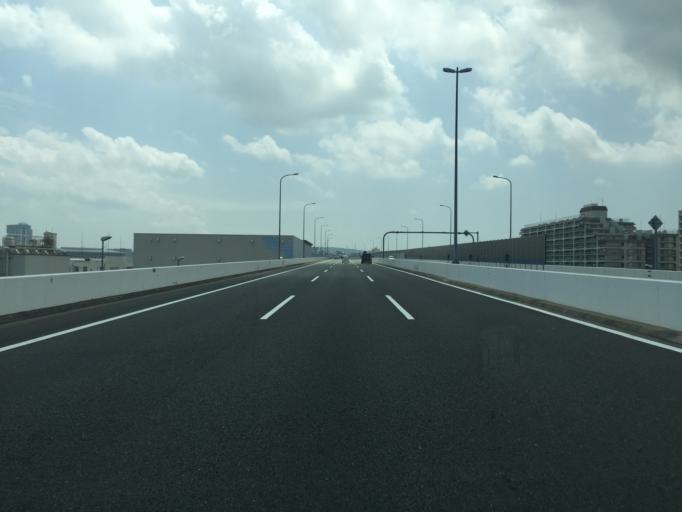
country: JP
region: Kanagawa
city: Yokohama
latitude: 35.4002
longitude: 139.6193
